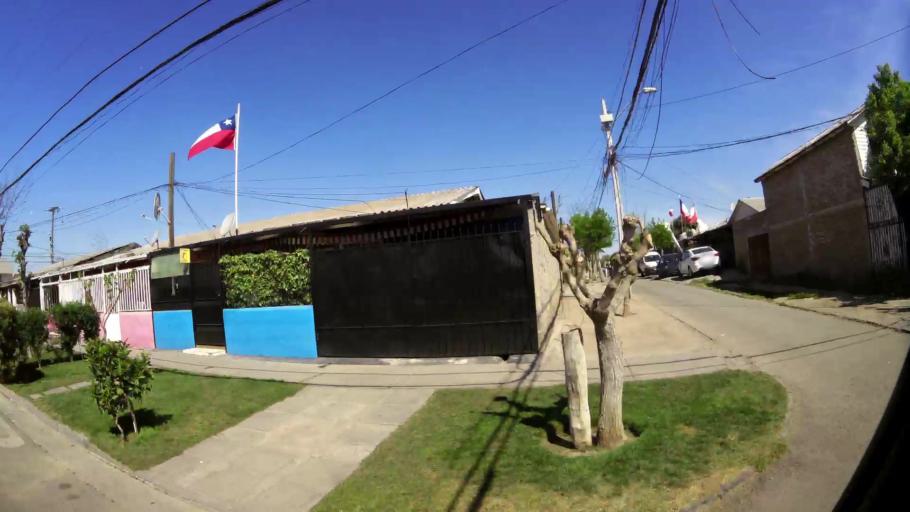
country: CL
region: Santiago Metropolitan
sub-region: Provincia de Santiago
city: Lo Prado
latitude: -33.4967
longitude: -70.7307
